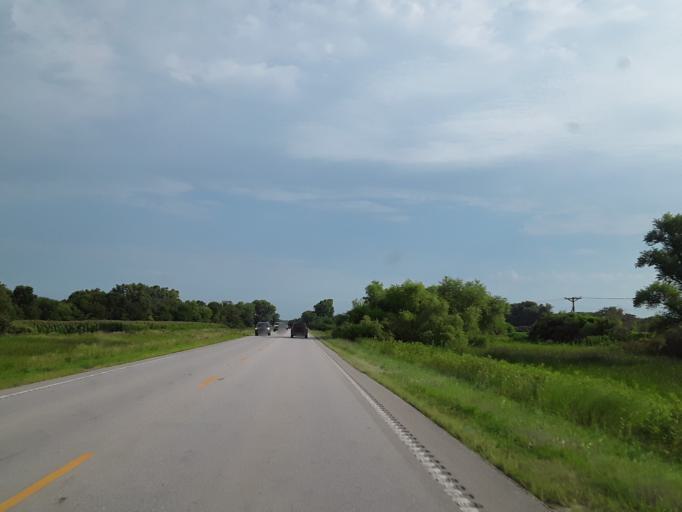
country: US
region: Nebraska
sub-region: Saunders County
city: Ashland
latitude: 41.0795
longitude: -96.3683
